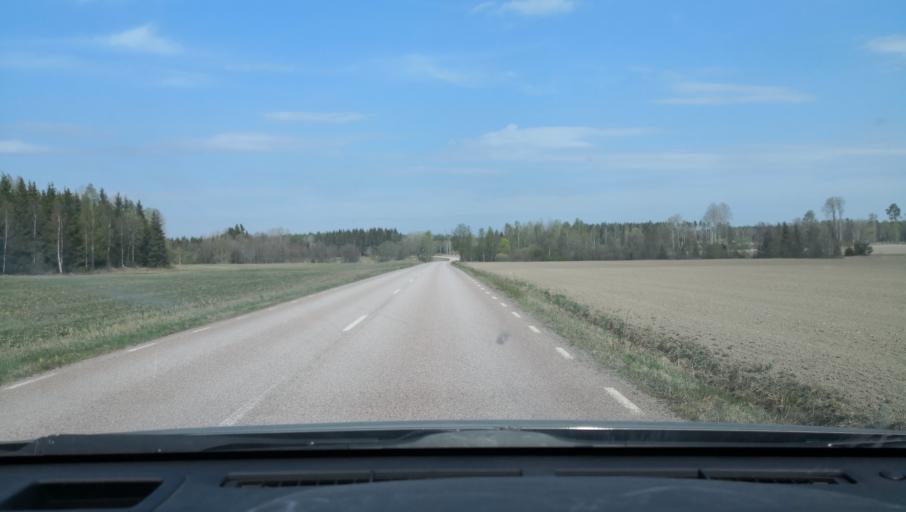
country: SE
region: Vaestmanland
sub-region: Vasteras
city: Skultuna
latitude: 59.7425
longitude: 16.4115
